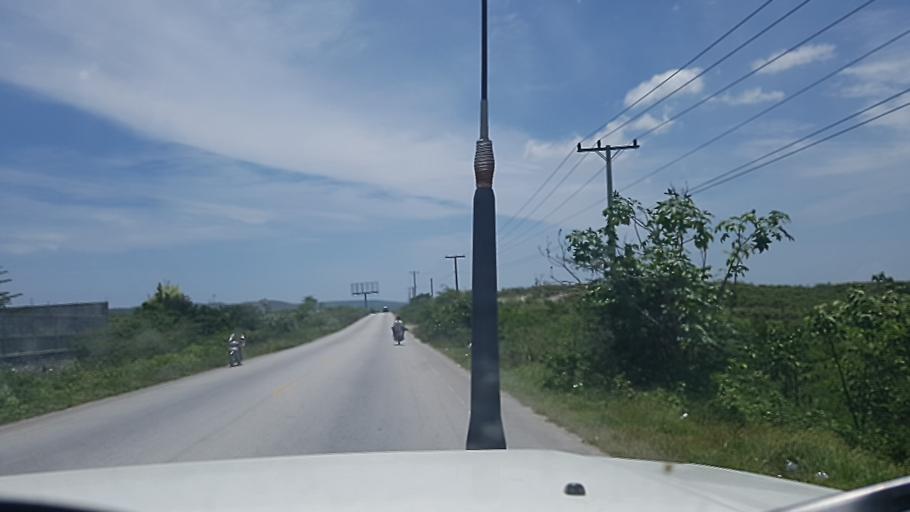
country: HT
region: Artibonite
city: Saint-Marc
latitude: 19.1519
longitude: -72.6309
